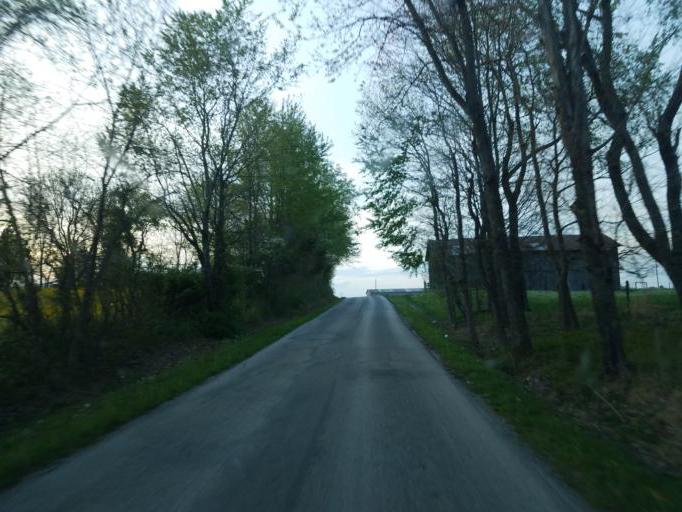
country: US
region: Kentucky
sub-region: Green County
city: Greensburg
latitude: 37.2078
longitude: -85.6944
